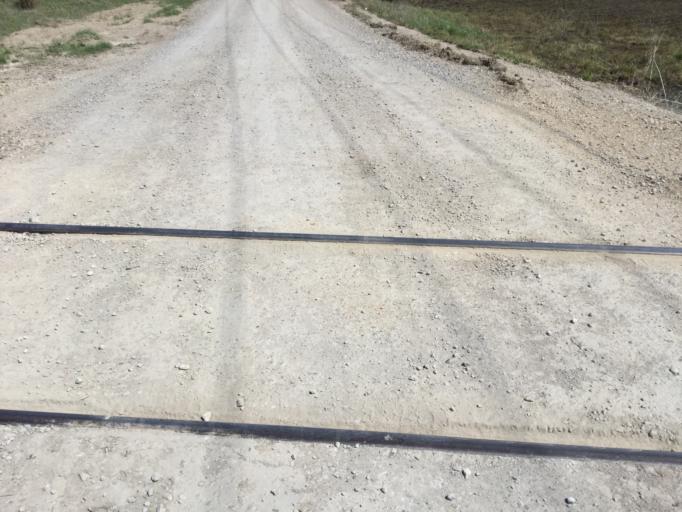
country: US
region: Kansas
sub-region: Neosho County
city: Chanute
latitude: 37.6308
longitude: -95.4670
